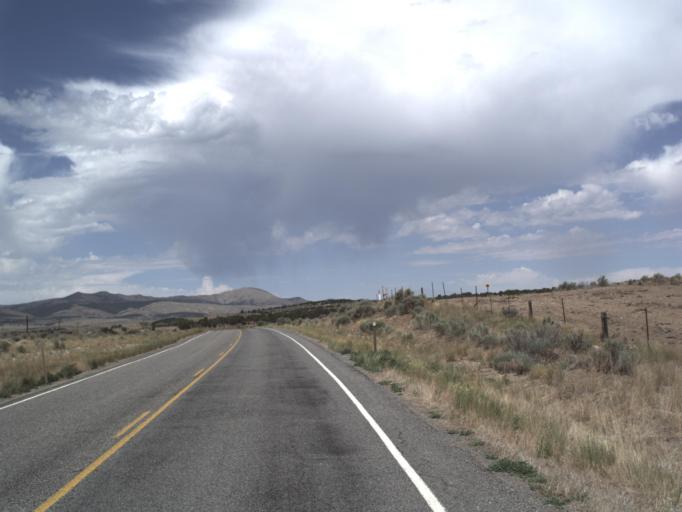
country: US
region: Utah
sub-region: Utah County
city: Genola
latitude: 39.9430
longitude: -112.1955
